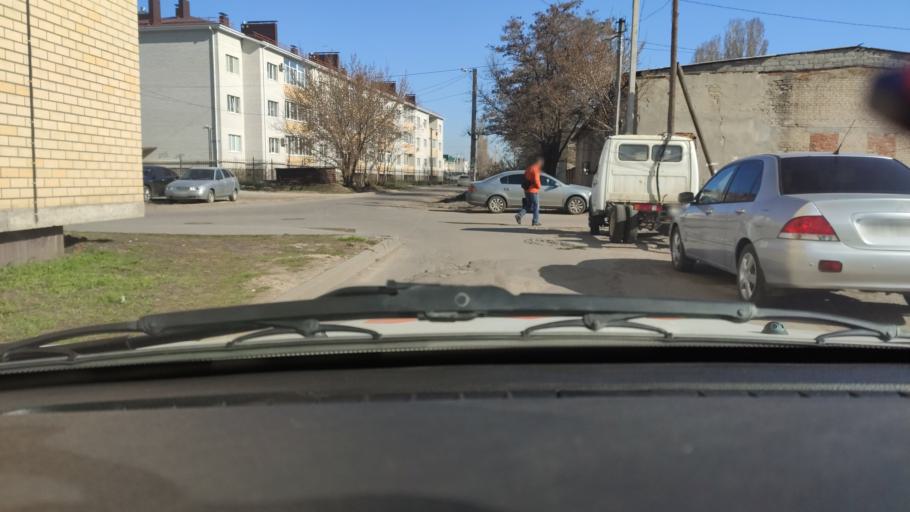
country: RU
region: Voronezj
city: Novaya Usman'
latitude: 51.6088
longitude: 39.3801
